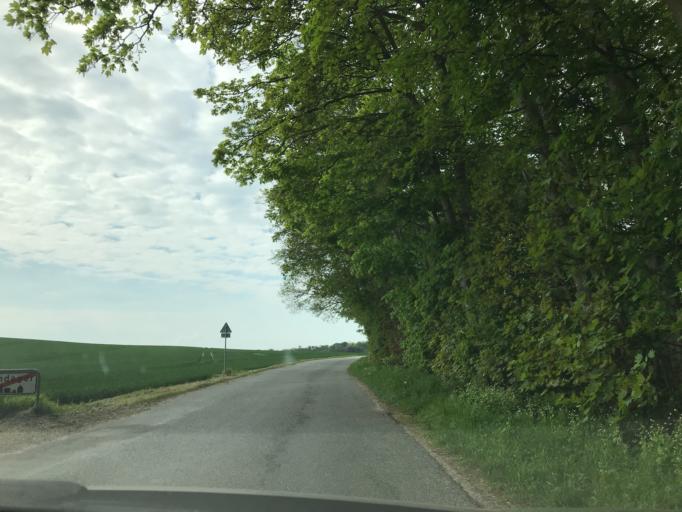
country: DK
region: South Denmark
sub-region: Assens Kommune
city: Assens
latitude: 55.3282
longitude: 9.9215
